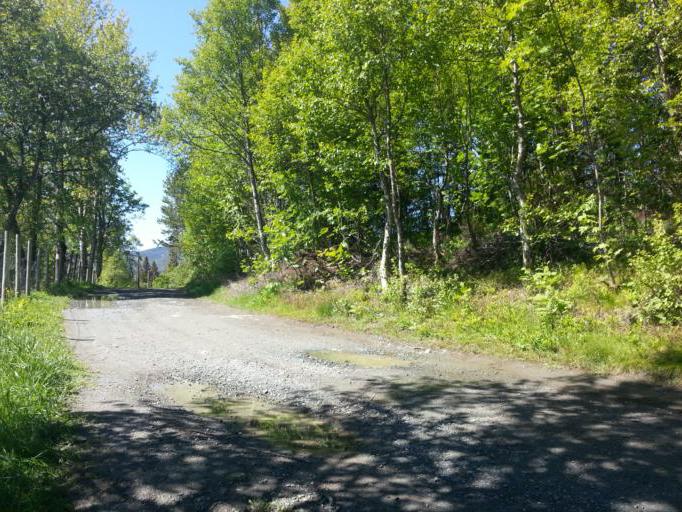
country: NO
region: Sor-Trondelag
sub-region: Trondheim
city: Trondheim
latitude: 63.3990
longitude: 10.3002
